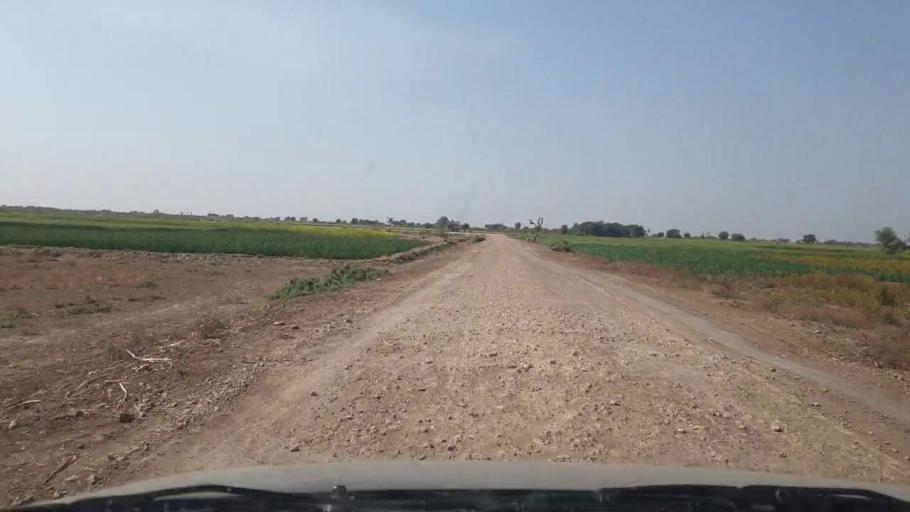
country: PK
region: Sindh
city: Samaro
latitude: 25.1938
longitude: 69.3453
